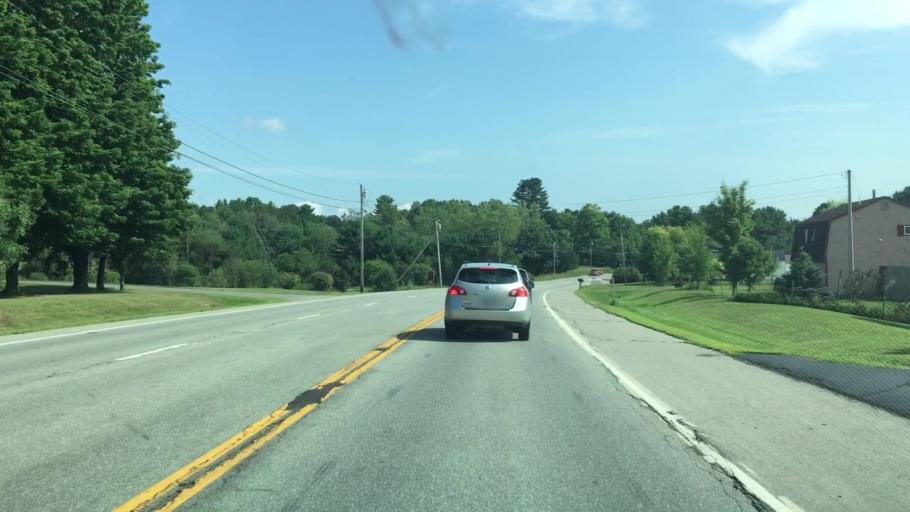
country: US
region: Maine
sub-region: Penobscot County
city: Orrington
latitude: 44.7048
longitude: -68.8453
